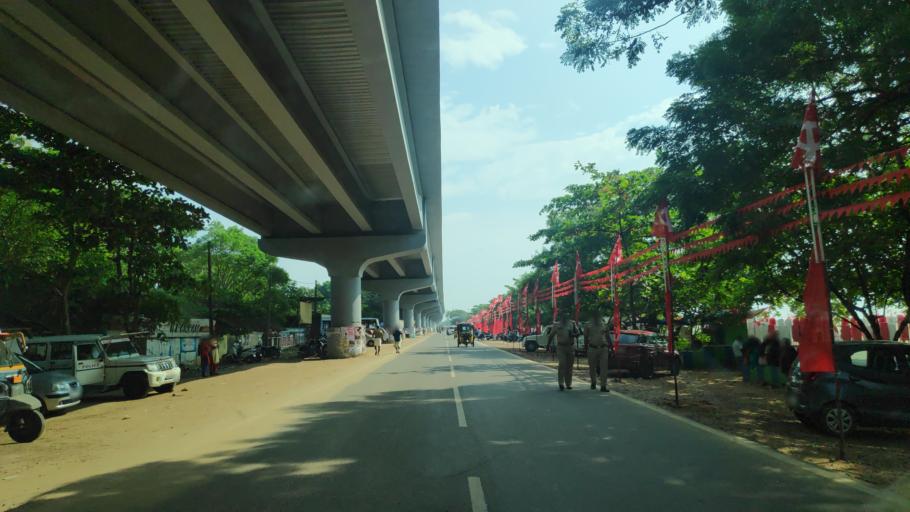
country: IN
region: Kerala
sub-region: Alappuzha
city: Alleppey
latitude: 9.4961
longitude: 76.3180
